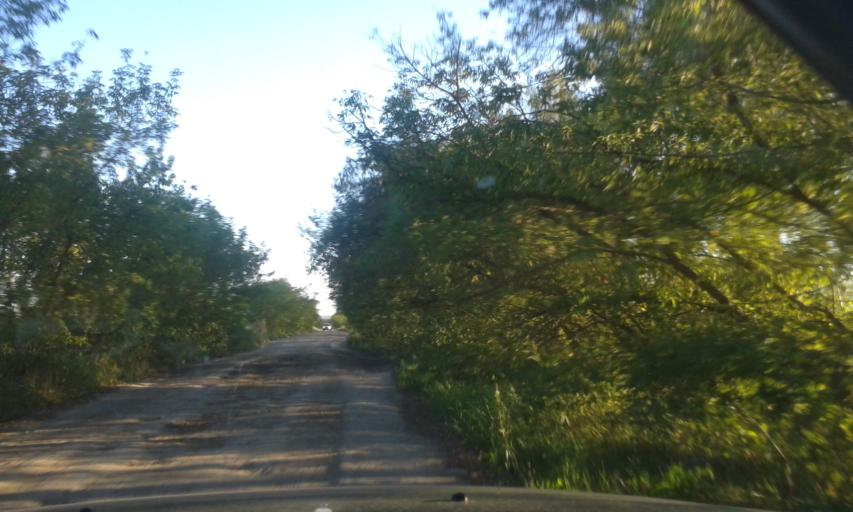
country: RU
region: Tula
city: Krapivna
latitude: 54.1305
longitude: 37.1569
